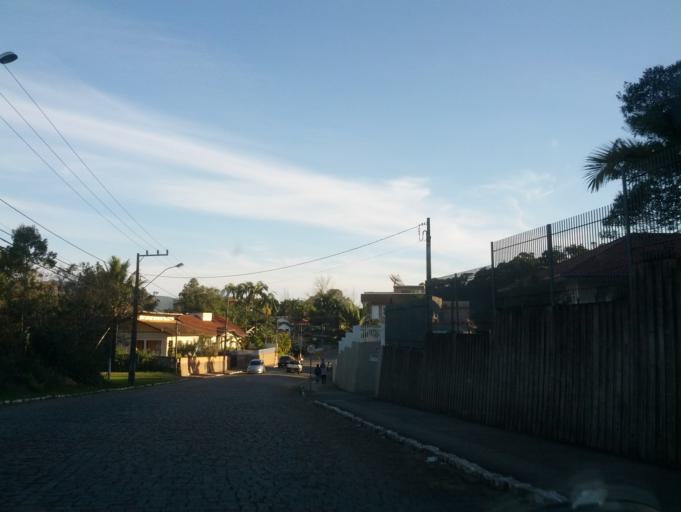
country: BR
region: Santa Catarina
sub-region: Indaial
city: Indaial
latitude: -26.8951
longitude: -49.2431
